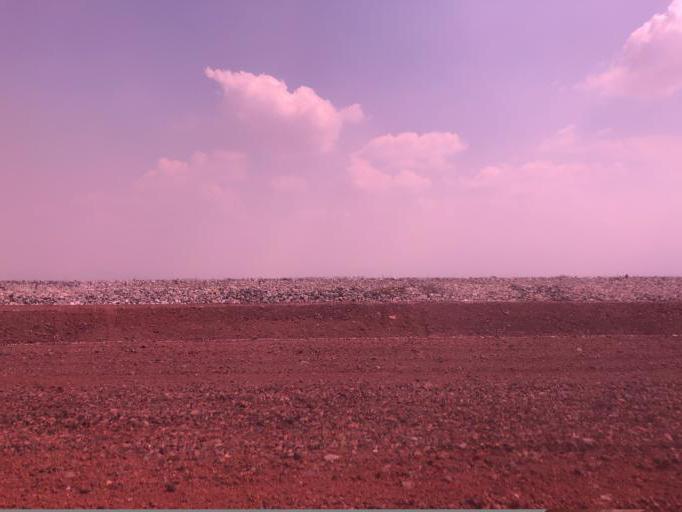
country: MX
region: Mexico
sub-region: Atenco
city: Colonia el Salado
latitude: 19.5431
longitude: -98.9940
